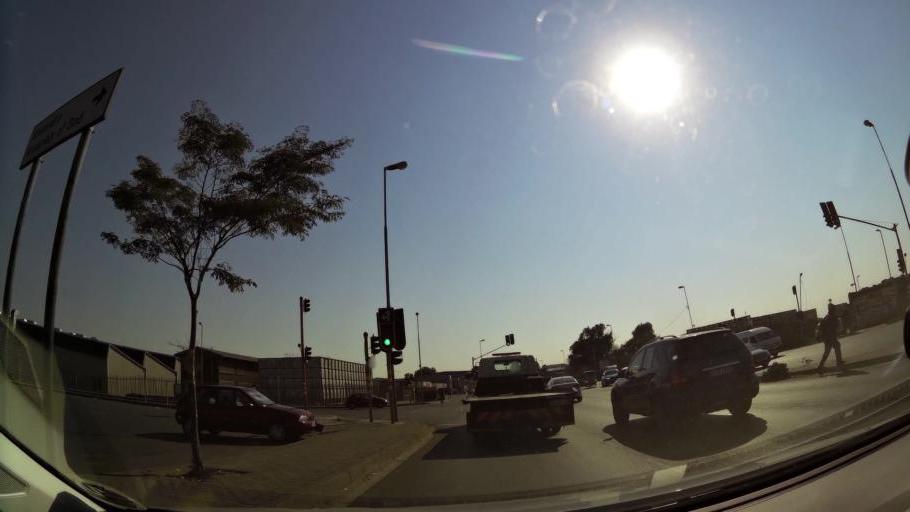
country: ZA
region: Gauteng
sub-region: City of Johannesburg Metropolitan Municipality
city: Modderfontein
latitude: -26.1014
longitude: 28.0854
